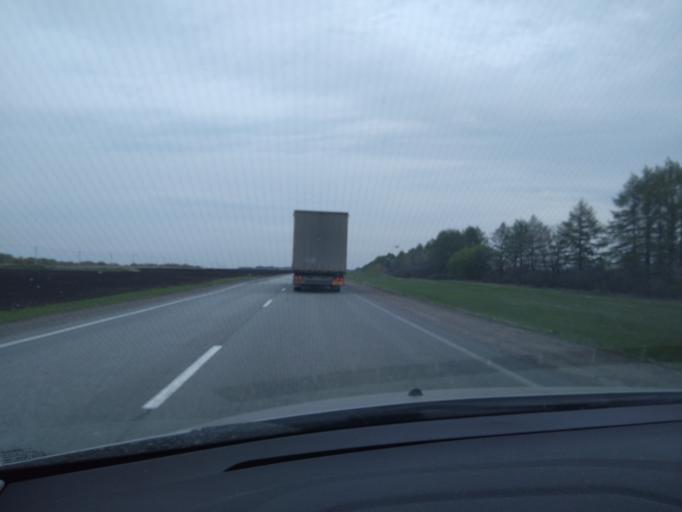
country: RU
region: Sverdlovsk
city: Yelanskiy
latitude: 56.7758
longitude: 62.4626
